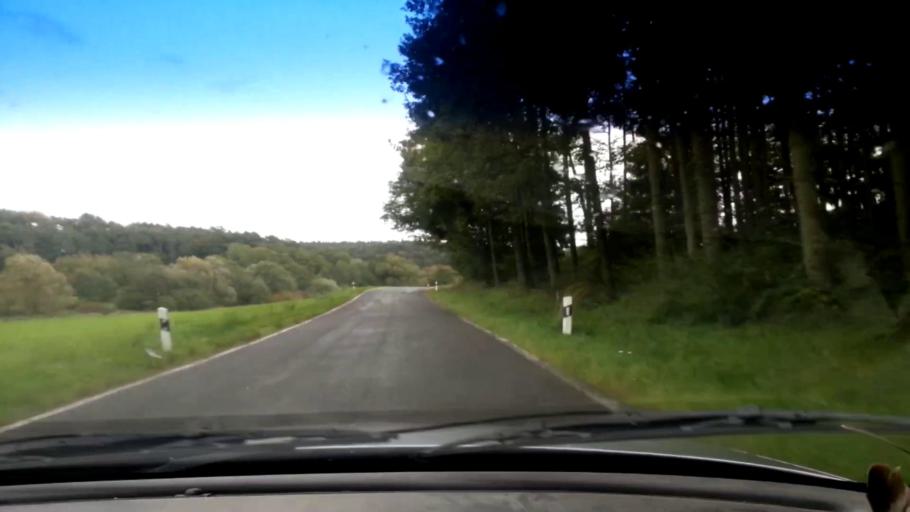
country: DE
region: Bavaria
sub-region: Regierungsbezirk Unterfranken
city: Kirchlauter
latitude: 50.0289
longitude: 10.7318
